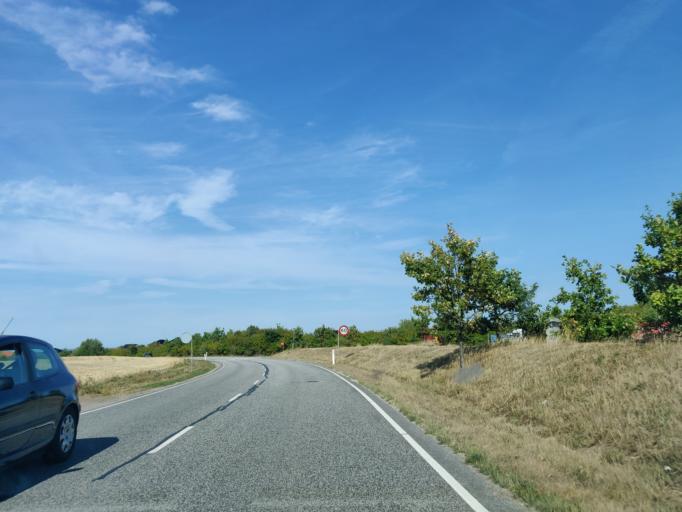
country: DK
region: Zealand
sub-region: Roskilde Kommune
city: Svogerslev
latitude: 55.6299
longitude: 12.0416
